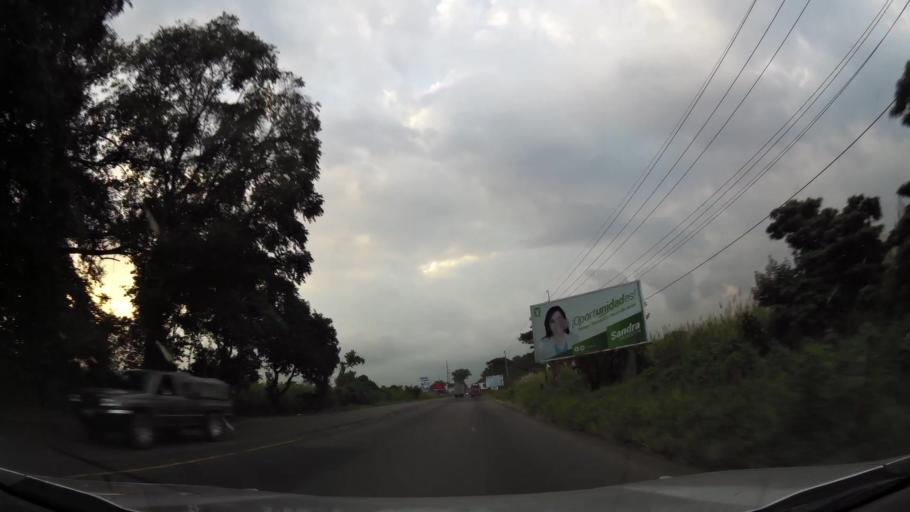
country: GT
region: Escuintla
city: Siquinala
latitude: 14.2940
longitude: -90.9440
